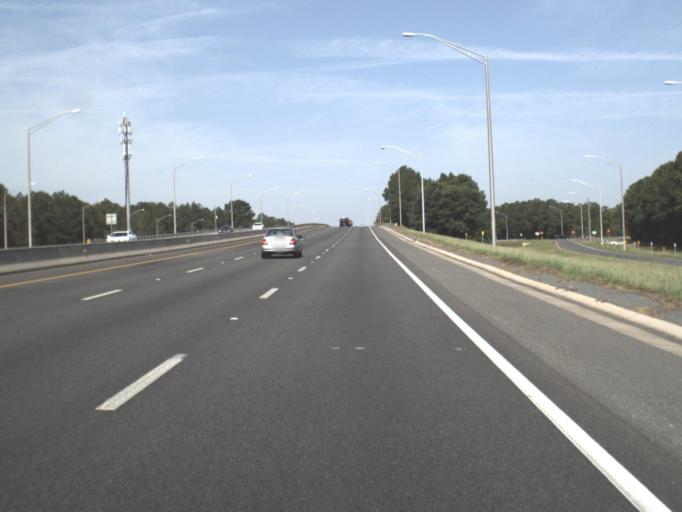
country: US
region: Florida
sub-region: Saint Johns County
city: Ponte Vedra Beach
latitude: 30.2518
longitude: -81.4625
